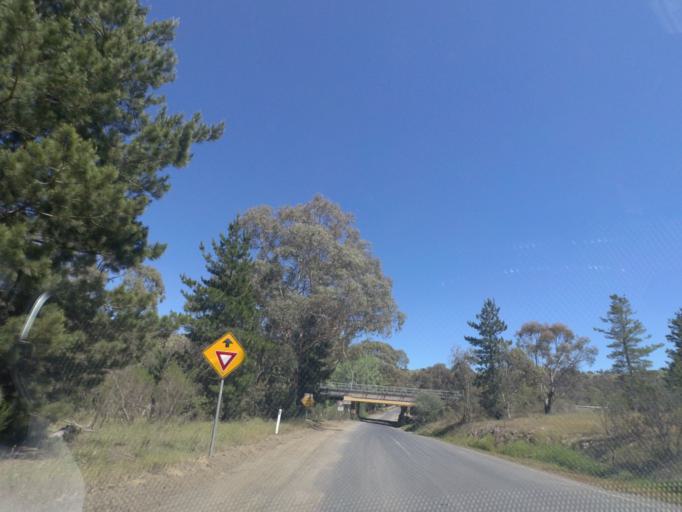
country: AU
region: Victoria
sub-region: Whittlesea
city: Whittlesea
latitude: -37.2887
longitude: 144.9834
